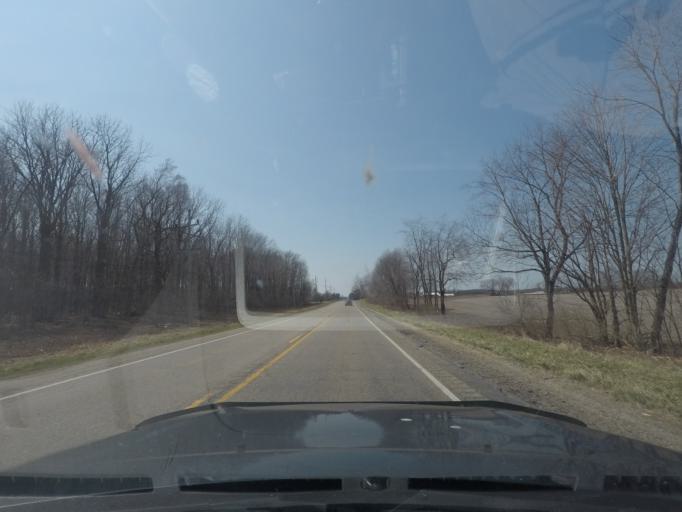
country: US
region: Indiana
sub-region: LaPorte County
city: LaPorte
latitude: 41.5914
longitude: -86.7753
